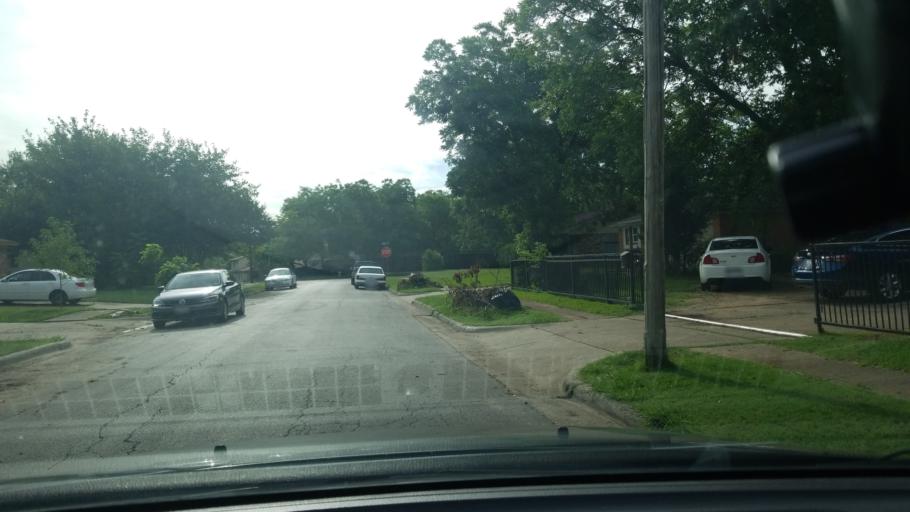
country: US
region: Texas
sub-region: Dallas County
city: Balch Springs
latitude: 32.7535
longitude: -96.6712
